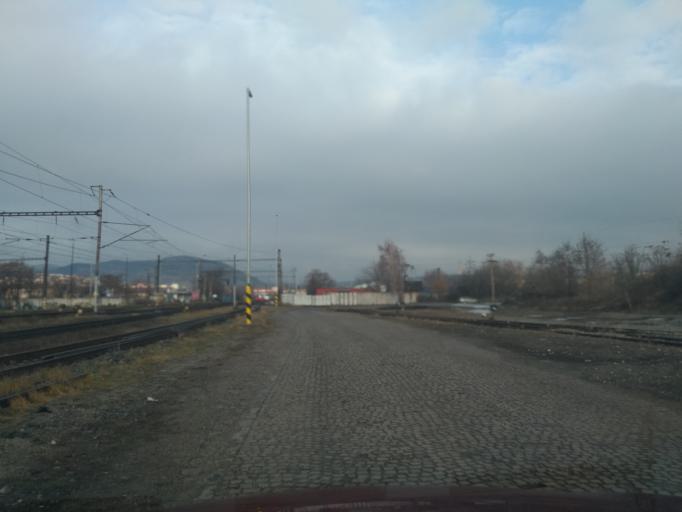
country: SK
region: Kosicky
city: Kosice
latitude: 48.7325
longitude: 21.2641
